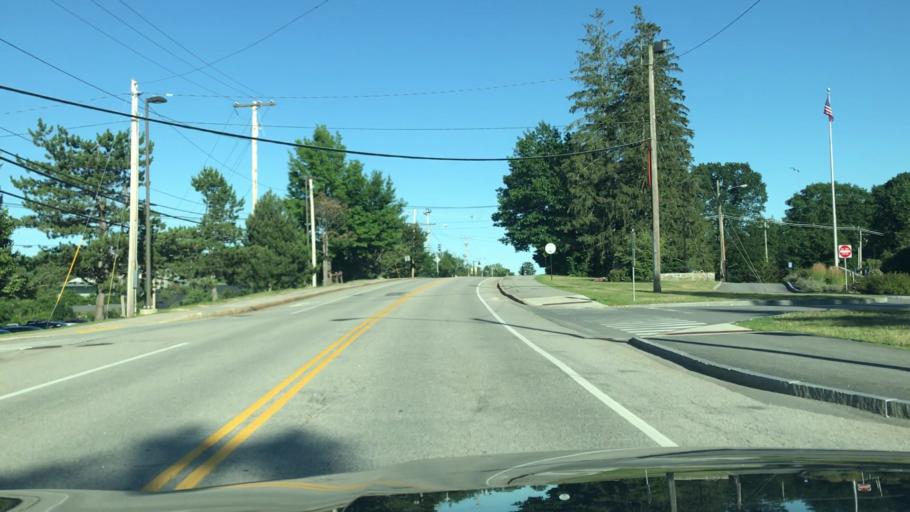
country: US
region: New Hampshire
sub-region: Strafford County
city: Durham
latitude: 43.1396
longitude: -70.9380
